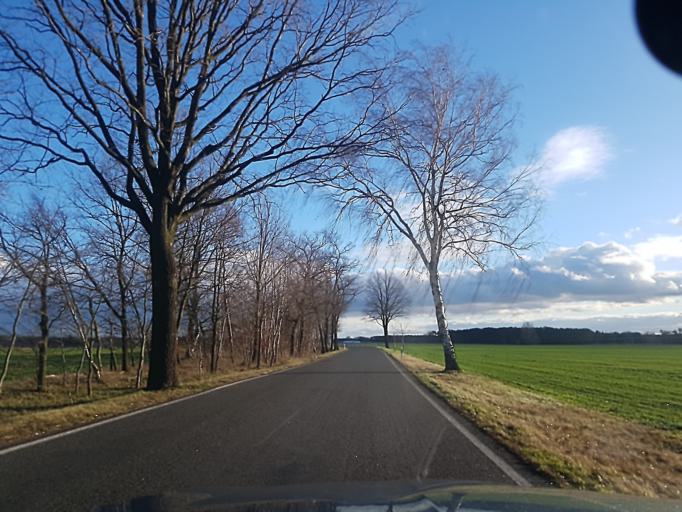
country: DE
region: Brandenburg
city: Schilda
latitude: 51.5599
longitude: 13.3475
